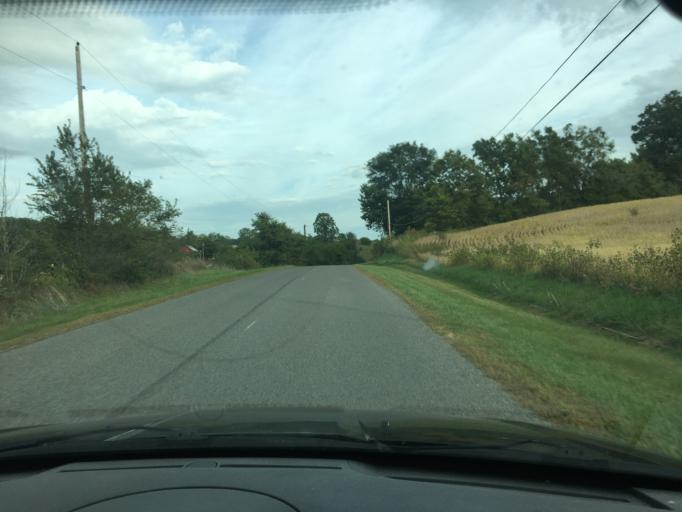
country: US
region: Ohio
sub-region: Logan County
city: West Liberty
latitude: 40.3019
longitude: -83.6929
